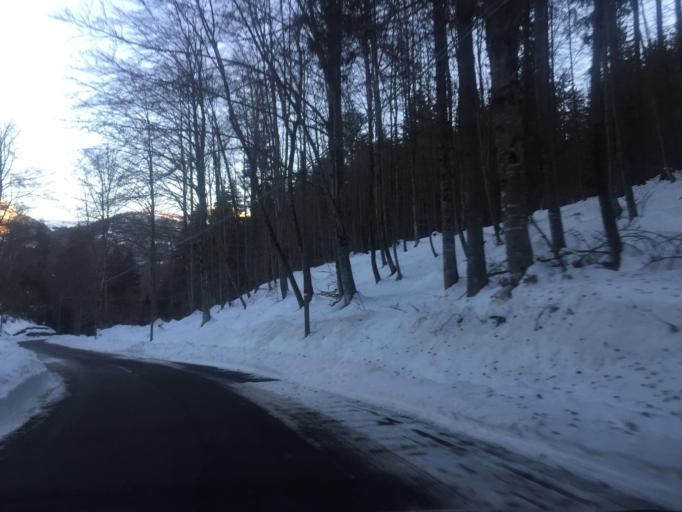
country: IT
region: Friuli Venezia Giulia
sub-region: Provincia di Udine
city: Lauco
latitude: 46.4302
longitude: 12.9483
